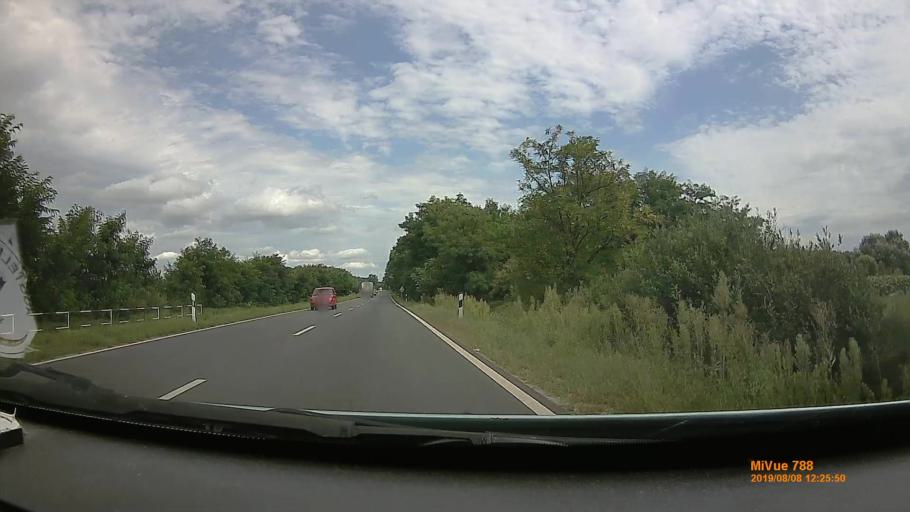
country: HU
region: Szabolcs-Szatmar-Bereg
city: Nyirbogat
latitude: 47.8133
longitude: 22.0780
